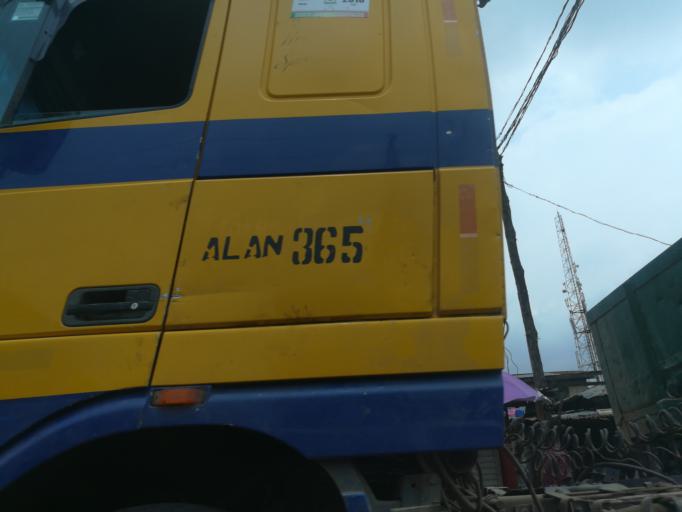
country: NG
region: Lagos
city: Agege
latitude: 6.6255
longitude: 3.3232
